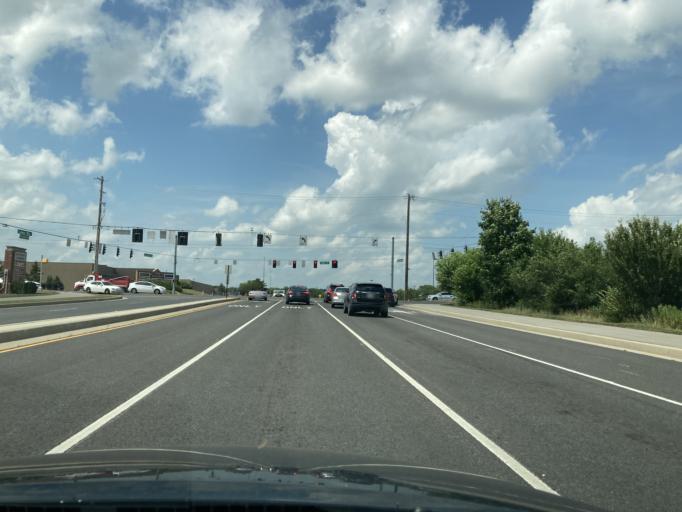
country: US
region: Indiana
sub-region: Hamilton County
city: Carmel
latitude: 39.9995
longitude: -86.1226
